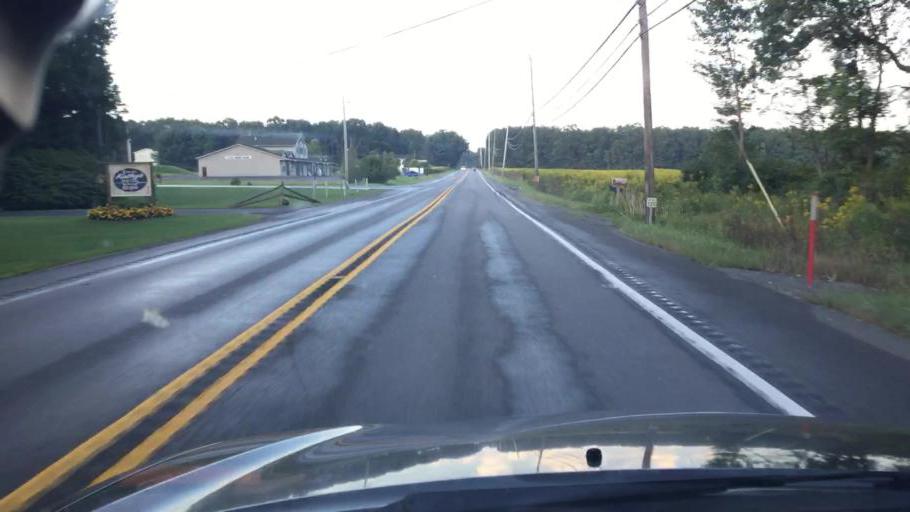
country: US
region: Pennsylvania
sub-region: Carbon County
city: Jim Thorpe
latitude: 40.9099
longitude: -75.6752
